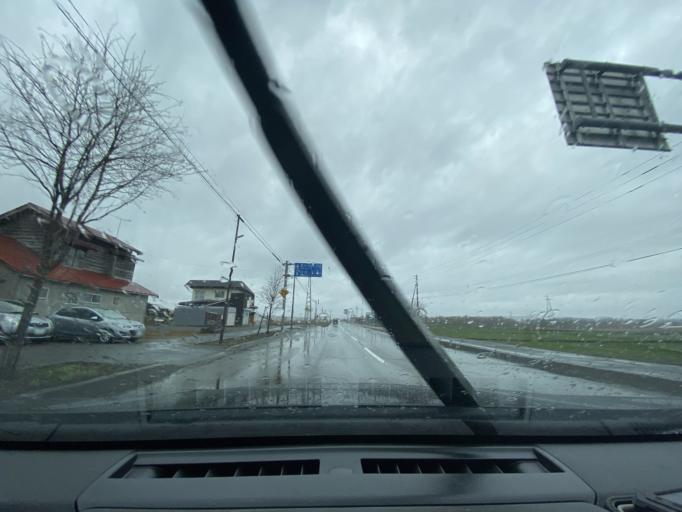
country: JP
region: Hokkaido
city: Fukagawa
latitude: 43.8090
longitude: 142.0213
